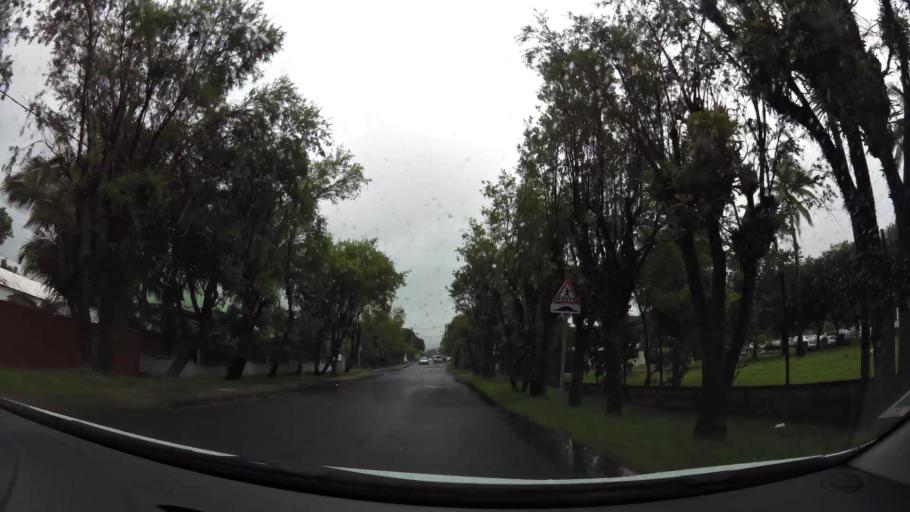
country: RE
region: Reunion
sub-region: Reunion
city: Saint-Andre
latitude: -20.9550
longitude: 55.6540
